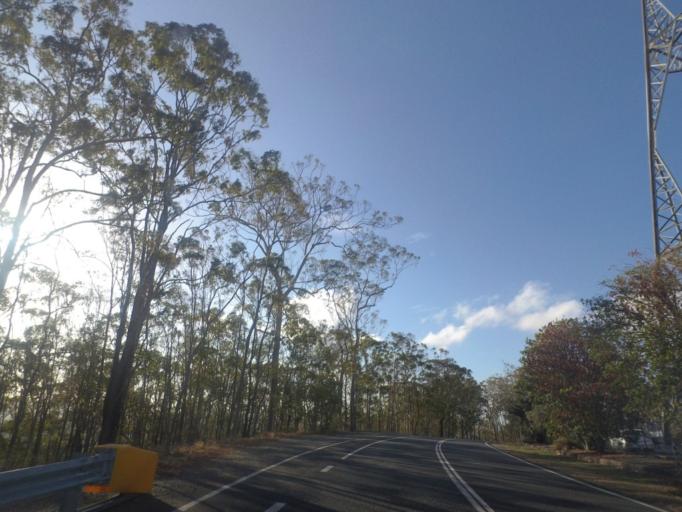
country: AU
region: Queensland
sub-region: Brisbane
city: Kenmore Hills
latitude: -27.4717
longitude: 152.9421
